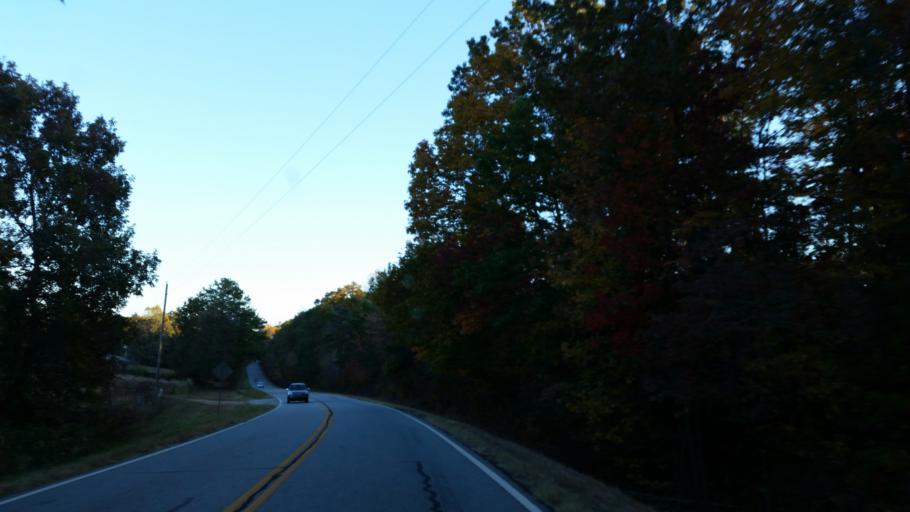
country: US
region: Georgia
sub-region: Lumpkin County
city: Dahlonega
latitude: 34.5279
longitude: -84.0564
